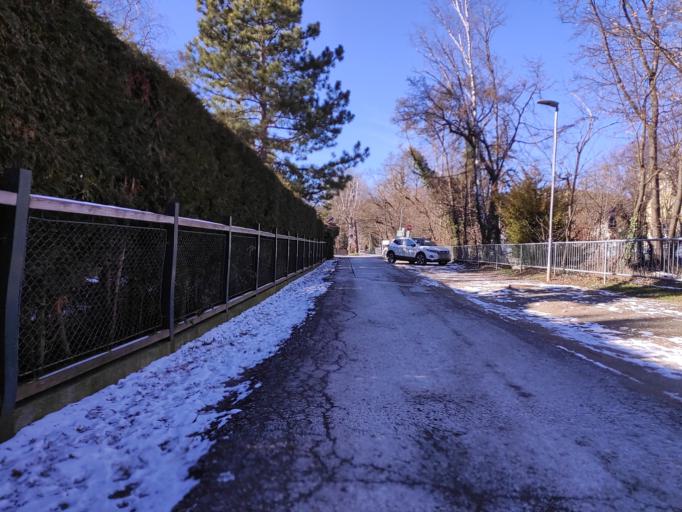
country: AT
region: Lower Austria
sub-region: Politischer Bezirk Modling
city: Hinterbruehl
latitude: 48.0861
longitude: 16.2563
